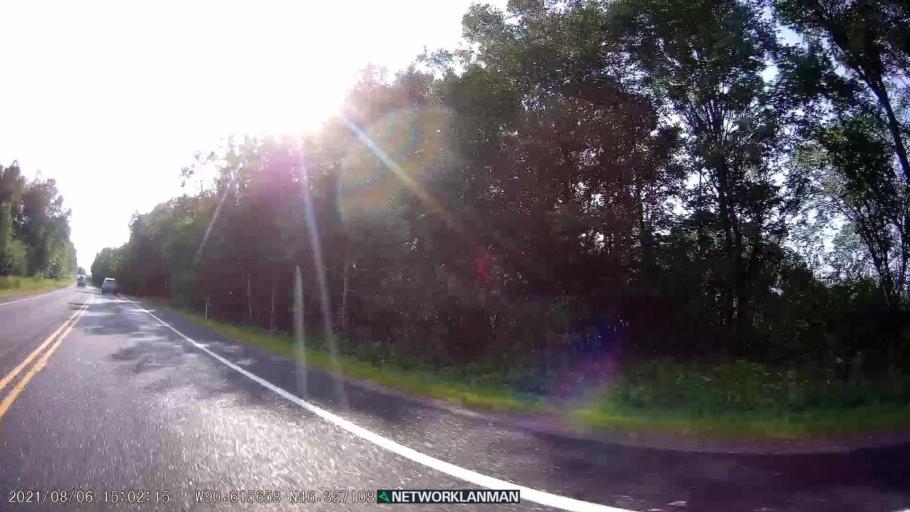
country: US
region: Wisconsin
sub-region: Ashland County
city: Ashland
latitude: 46.3265
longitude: -90.6162
